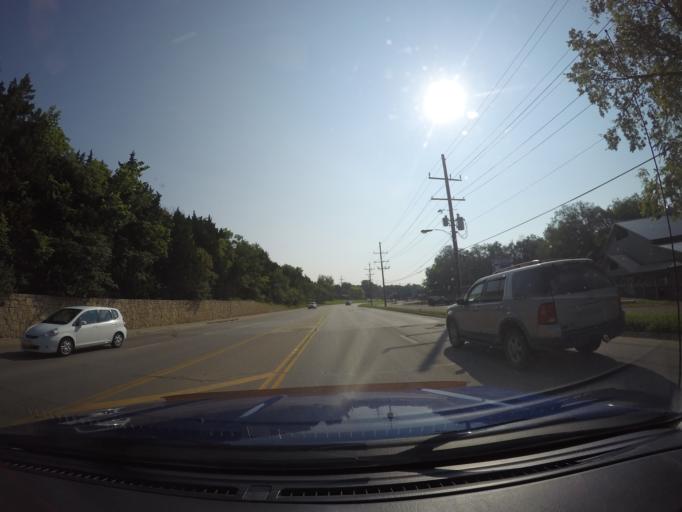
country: US
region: Kansas
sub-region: Riley County
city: Manhattan
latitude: 39.1737
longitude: -96.5900
